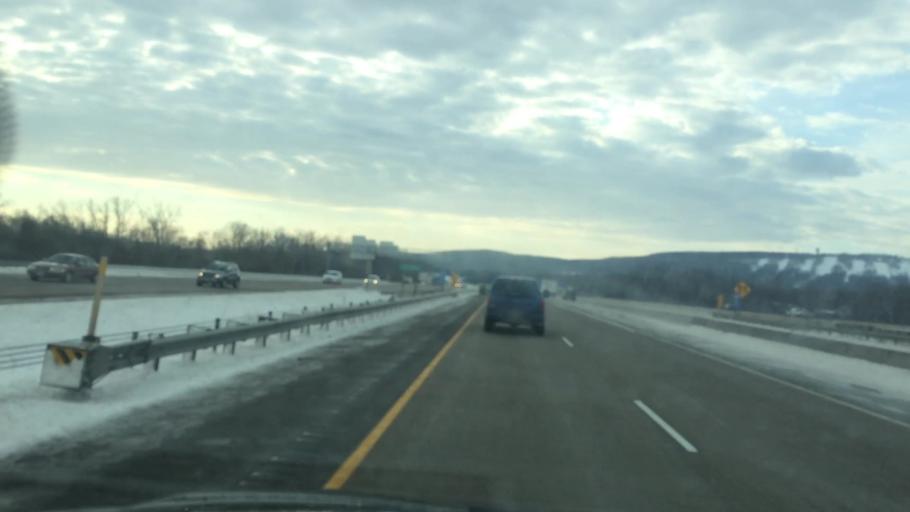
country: US
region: Wisconsin
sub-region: Marathon County
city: Rib Mountain
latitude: 44.9469
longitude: -89.6667
